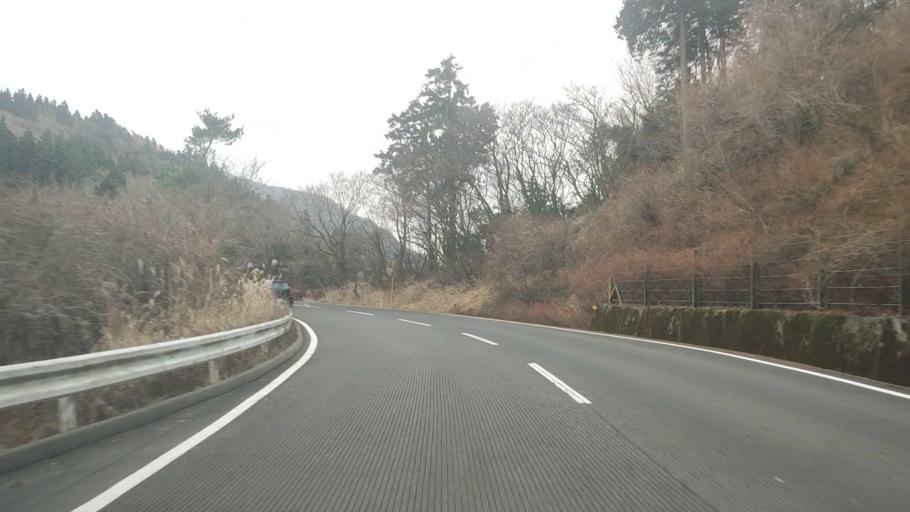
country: JP
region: Nagasaki
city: Shimabara
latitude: 32.7653
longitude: 130.2723
